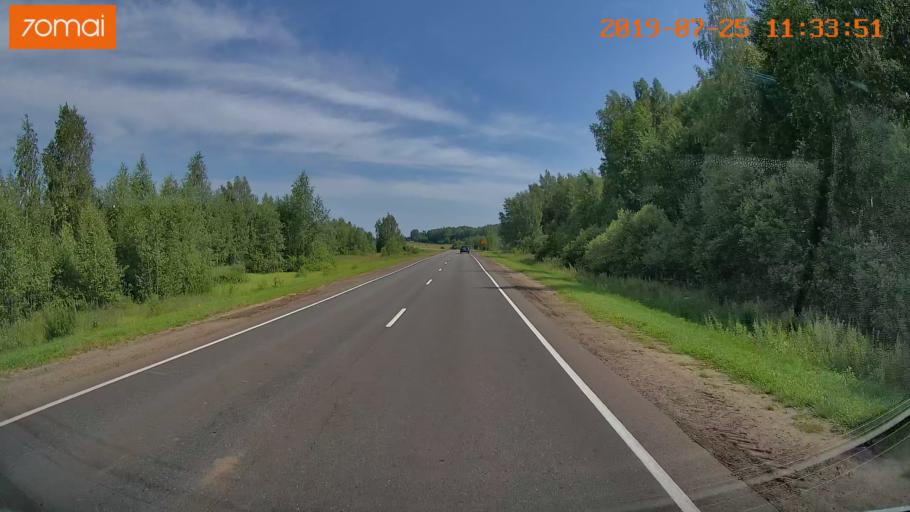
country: RU
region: Ivanovo
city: Privolzhsk
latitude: 57.3959
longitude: 41.4037
